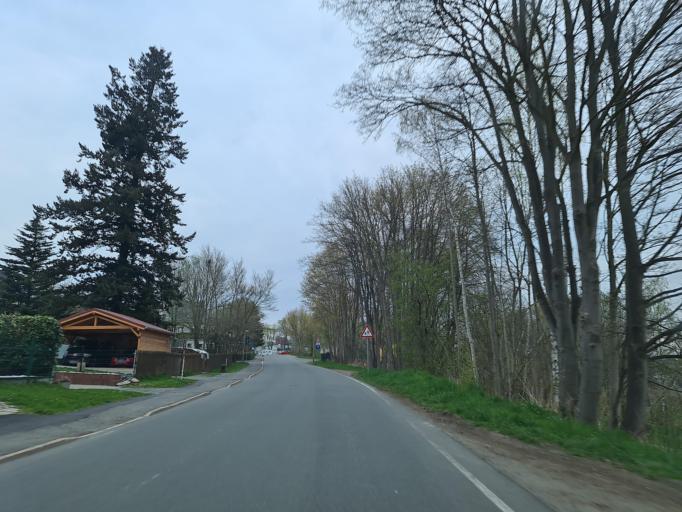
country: DE
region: Saxony
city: Falkenstein
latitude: 50.4731
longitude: 12.3750
